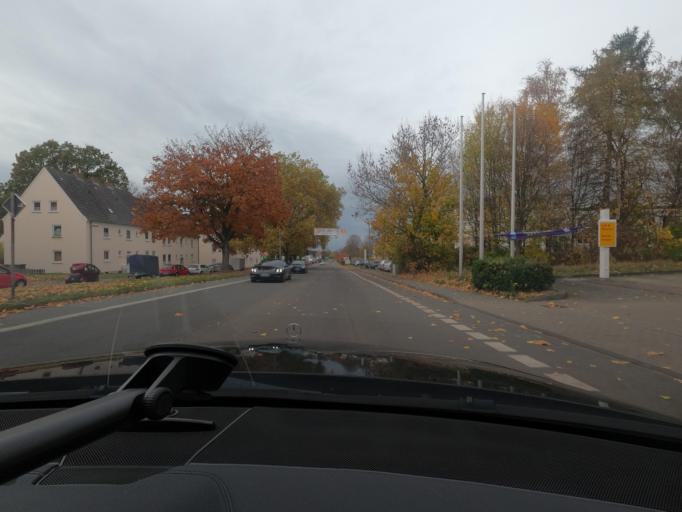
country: DE
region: North Rhine-Westphalia
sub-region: Regierungsbezirk Arnsberg
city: Soest
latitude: 51.5585
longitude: 8.1276
